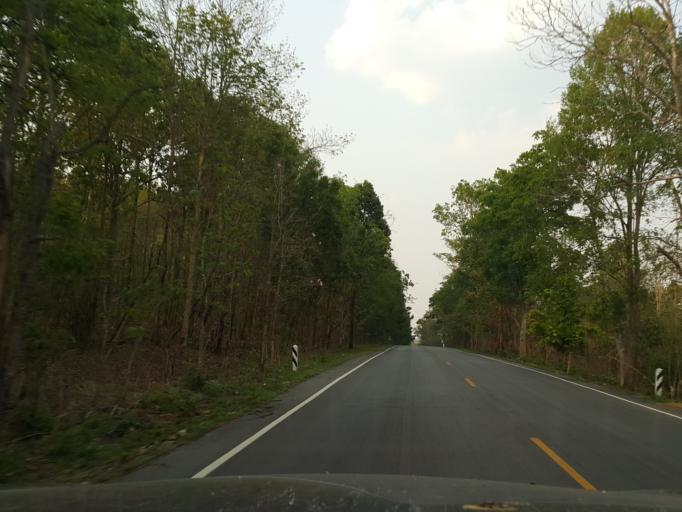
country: TH
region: Lamphun
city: Li
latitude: 17.8487
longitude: 99.0213
